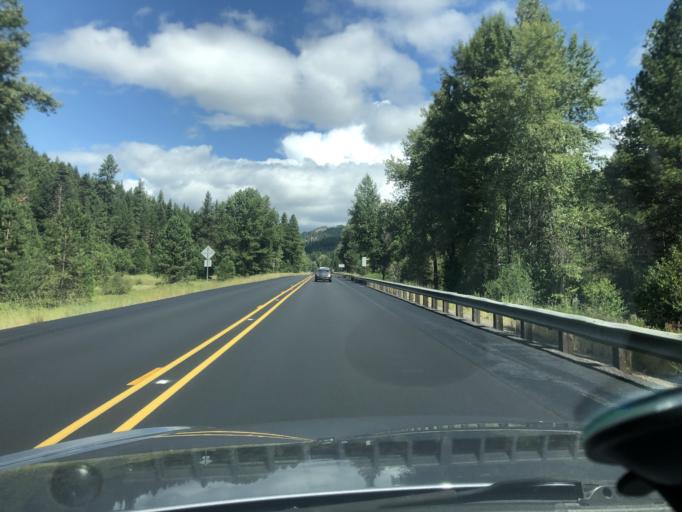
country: US
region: Washington
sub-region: Kittitas County
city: Cle Elum
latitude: 47.3054
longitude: -120.6952
